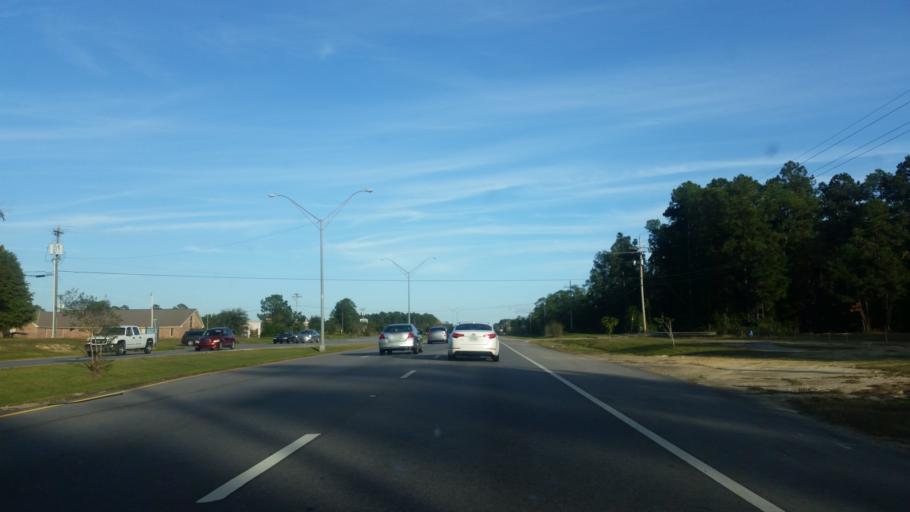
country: US
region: Mississippi
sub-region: Jackson County
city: Gulf Park Estates
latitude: 30.4067
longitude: -88.7458
